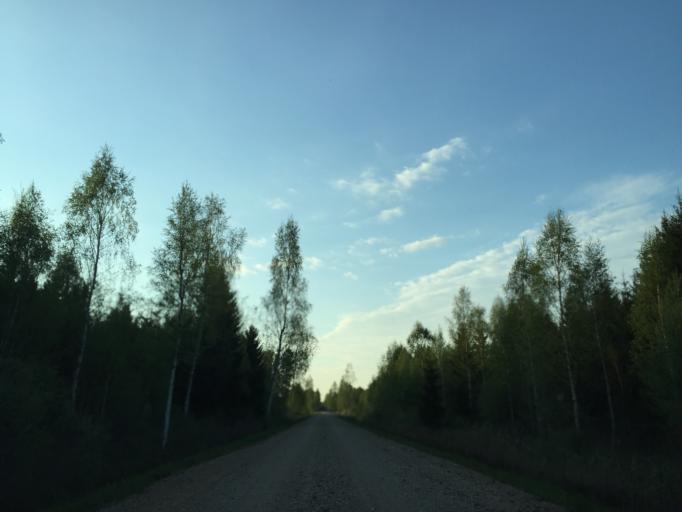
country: LV
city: Tireli
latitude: 56.8511
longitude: 23.6943
